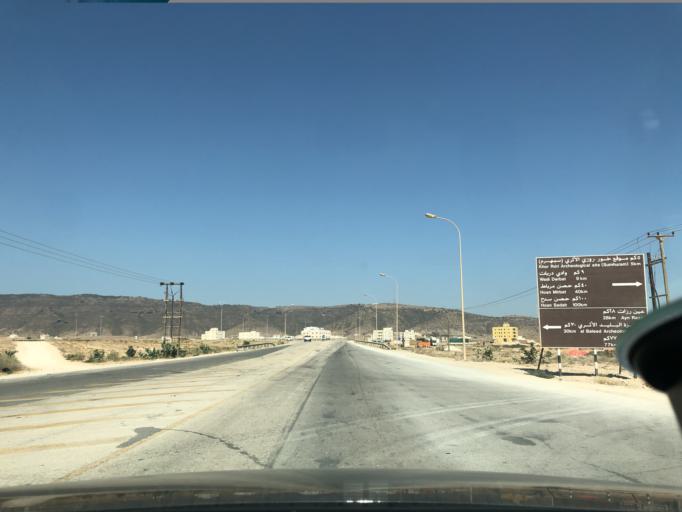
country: OM
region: Zufar
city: Salalah
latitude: 17.0466
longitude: 54.3998
